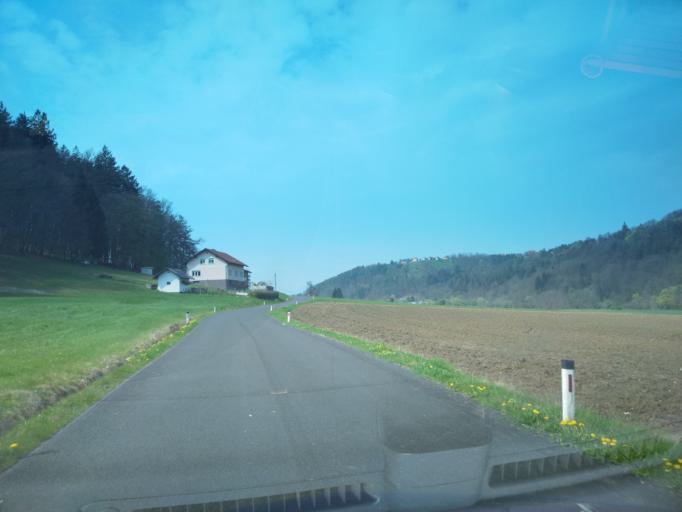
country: AT
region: Styria
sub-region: Politischer Bezirk Leibnitz
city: Kitzeck im Sausal
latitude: 46.7549
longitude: 15.4164
